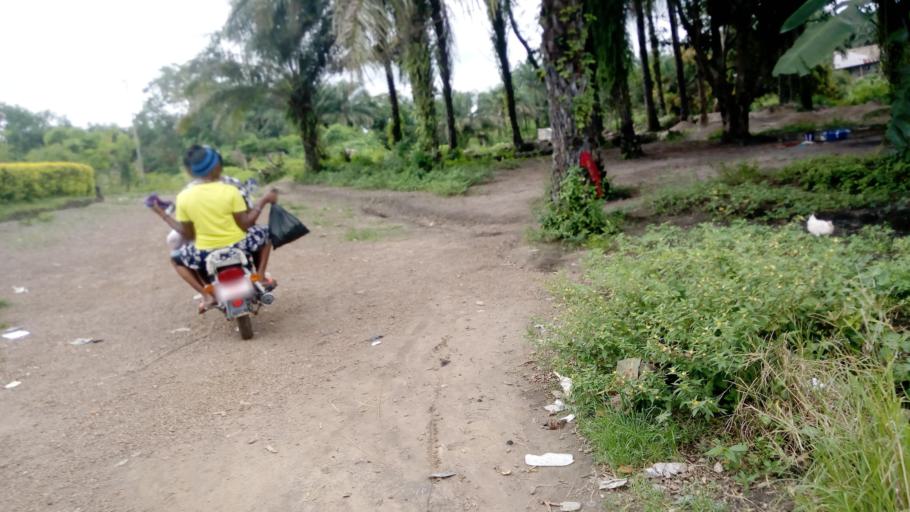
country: SL
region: Northern Province
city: Makeni
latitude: 8.8959
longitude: -12.0270
